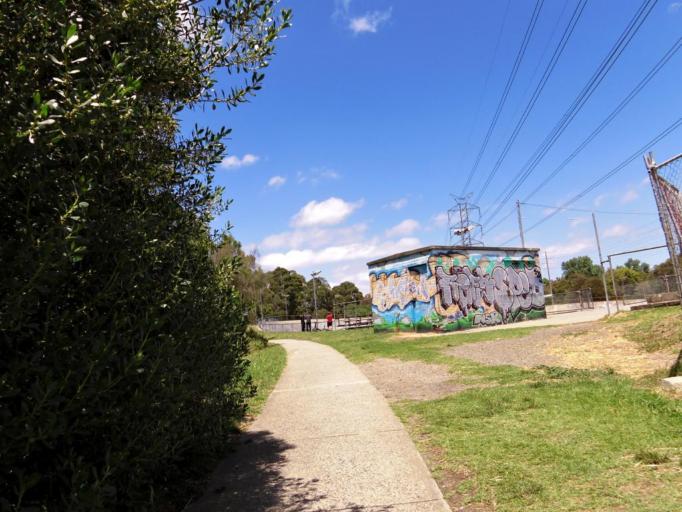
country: AU
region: Victoria
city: Brunswick East
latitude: -37.7605
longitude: 144.9817
